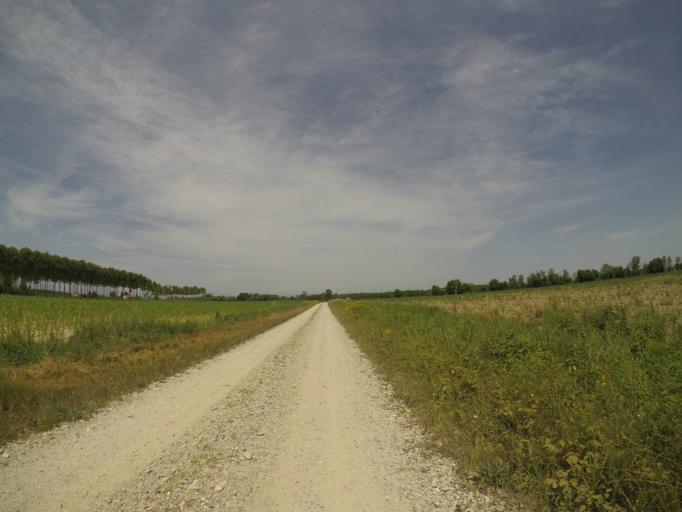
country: IT
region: Friuli Venezia Giulia
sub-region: Provincia di Udine
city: Camino al Tagliamento
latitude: 45.9084
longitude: 12.9592
